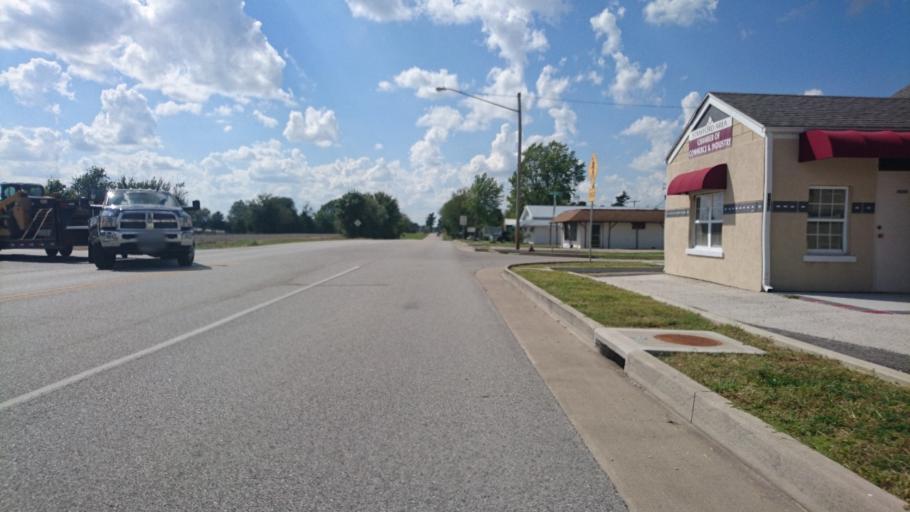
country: US
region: Missouri
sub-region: Greene County
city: Strafford
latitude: 37.2684
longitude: -93.1182
